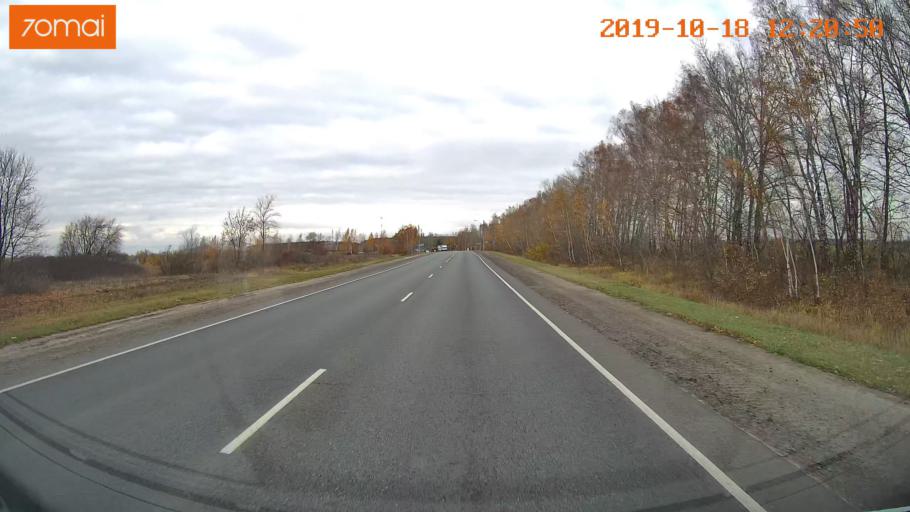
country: RU
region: Rjazan
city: Bagramovo
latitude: 54.5038
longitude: 39.4851
